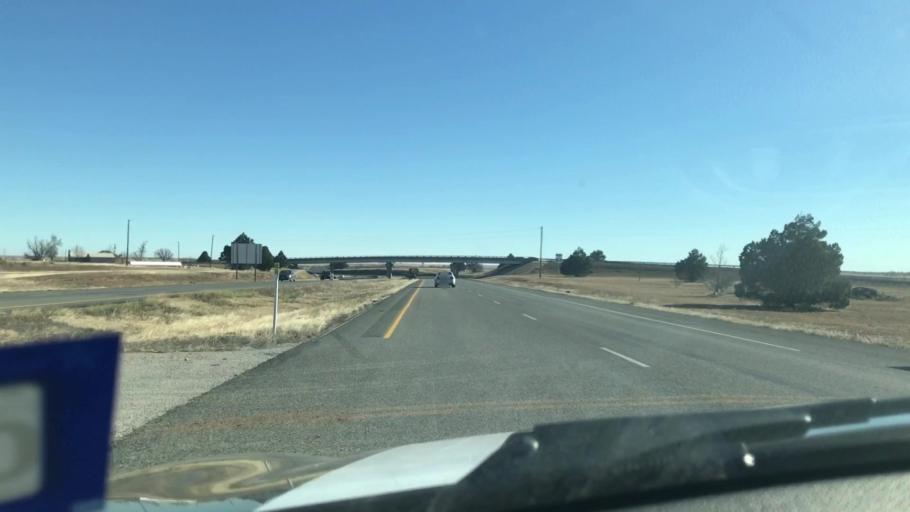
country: US
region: Texas
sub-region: Scurry County
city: Snyder
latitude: 32.6933
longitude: -100.8606
